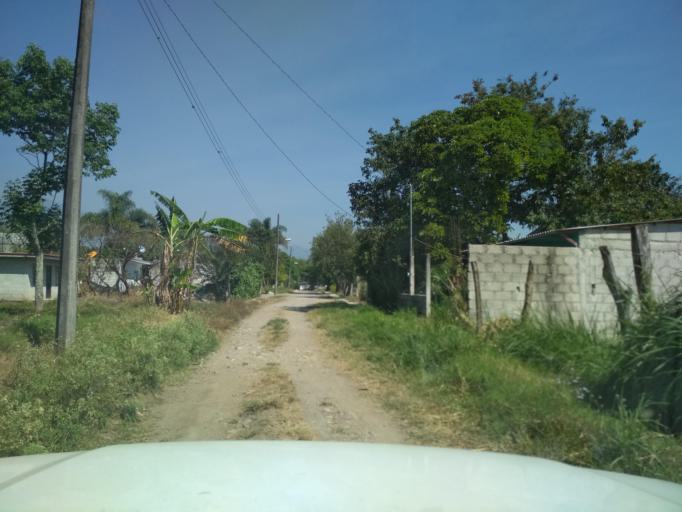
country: MX
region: Veracruz
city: Jalapilla
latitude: 18.8154
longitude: -97.0849
